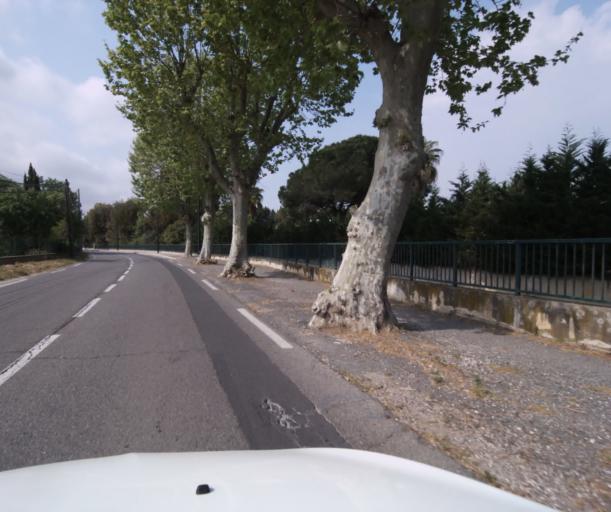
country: FR
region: Provence-Alpes-Cote d'Azur
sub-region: Departement du Var
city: Hyeres
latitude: 43.1085
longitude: 6.1397
